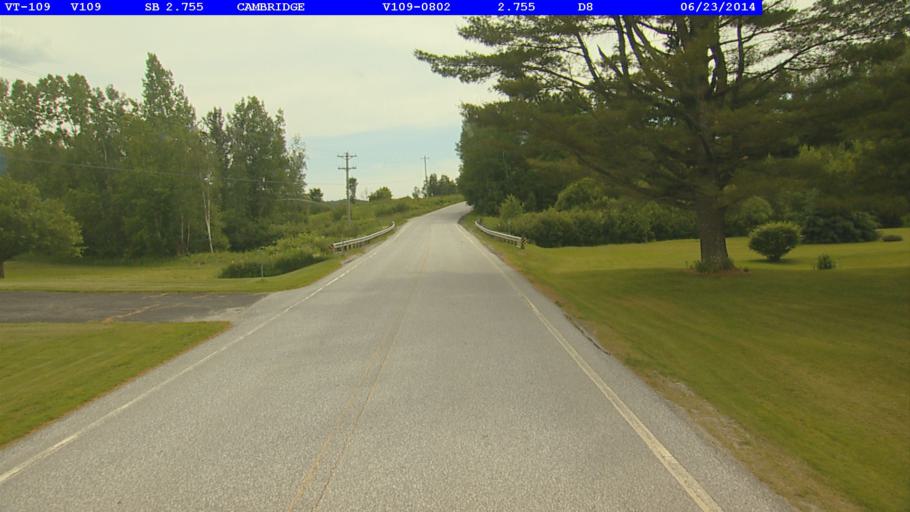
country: US
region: Vermont
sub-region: Lamoille County
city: Johnson
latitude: 44.6753
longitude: -72.7889
